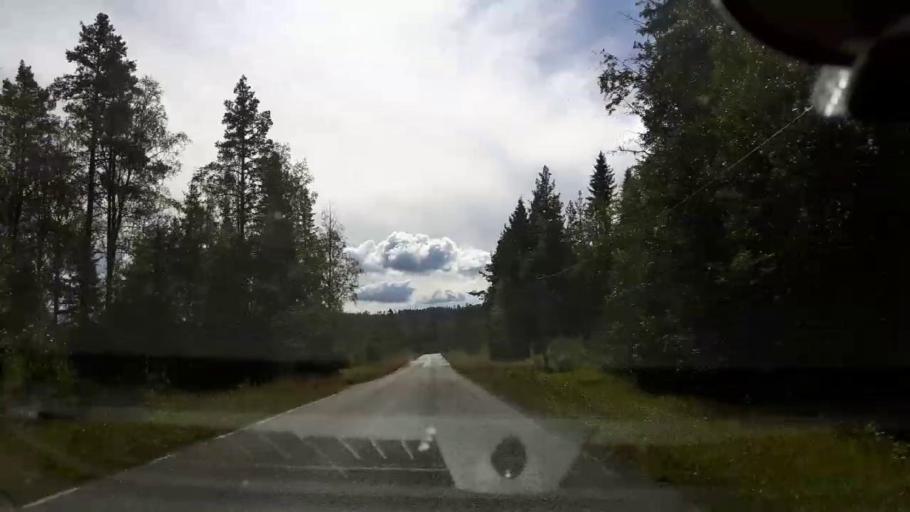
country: SE
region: Jaemtland
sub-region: Braecke Kommun
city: Braecke
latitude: 63.1963
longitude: 15.3687
